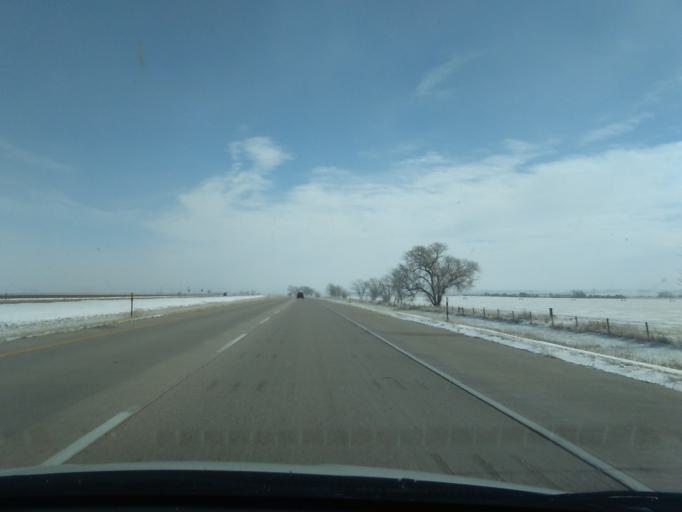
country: US
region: Wyoming
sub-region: Laramie County
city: Pine Bluffs
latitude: 41.1495
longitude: -104.1900
